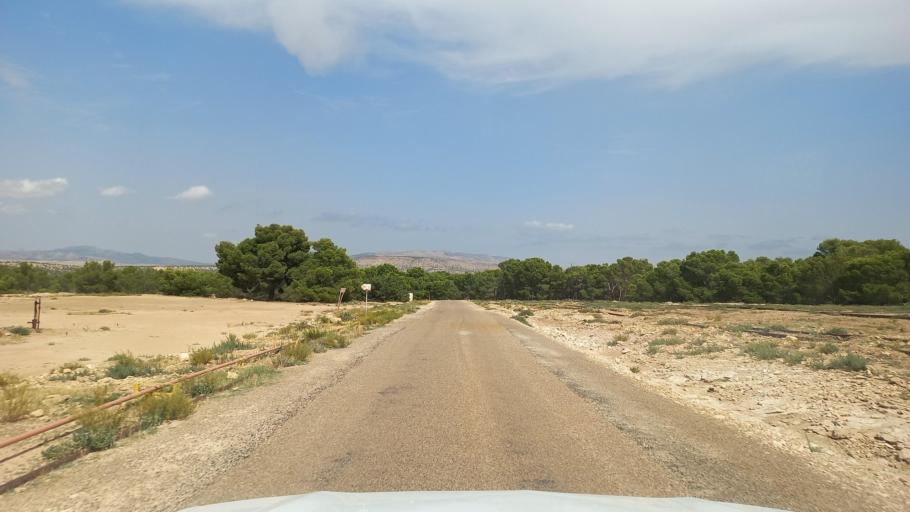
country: TN
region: Al Qasrayn
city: Sbiba
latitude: 35.3875
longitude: 8.9053
